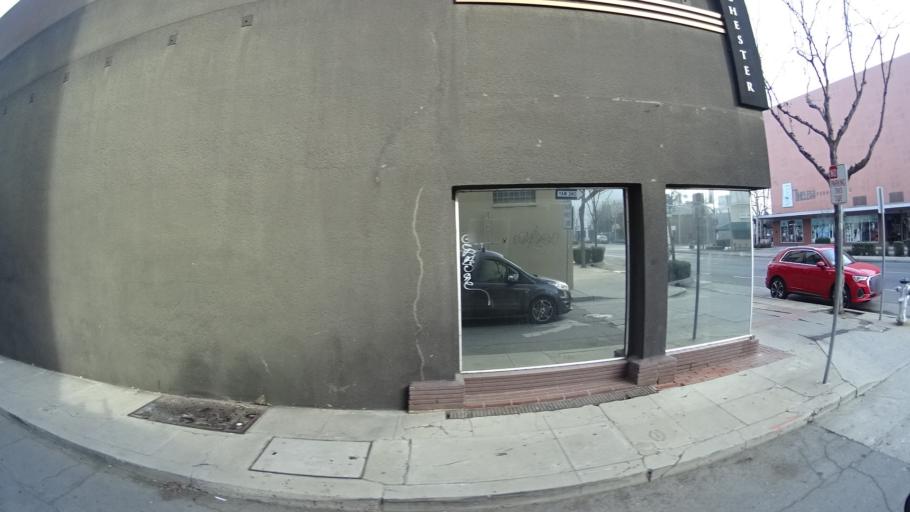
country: US
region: California
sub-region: Kern County
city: Bakersfield
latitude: 35.3767
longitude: -119.0191
